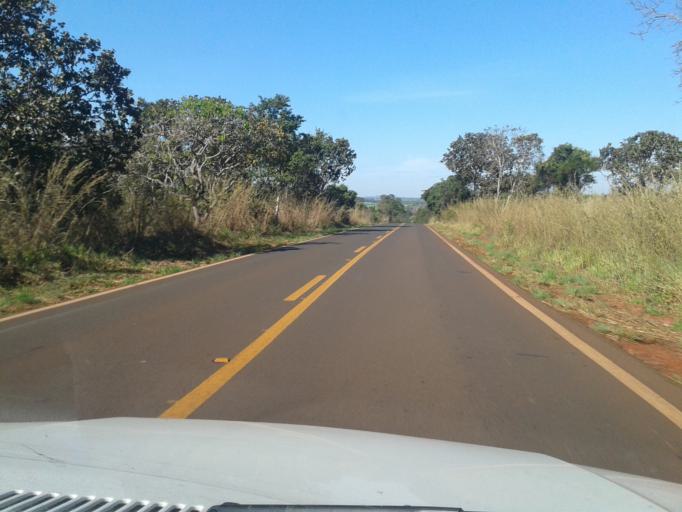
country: BR
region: Minas Gerais
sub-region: Ituiutaba
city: Ituiutaba
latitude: -19.0692
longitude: -49.7662
